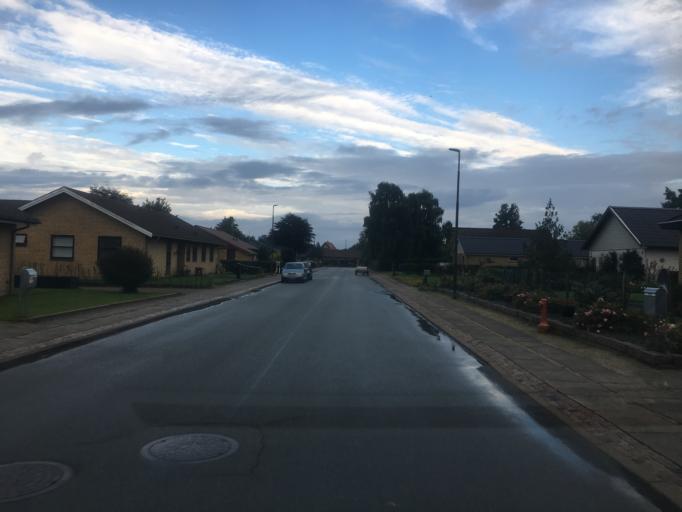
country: DK
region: South Denmark
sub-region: Tonder Kommune
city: Tonder
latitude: 54.9436
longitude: 8.8835
